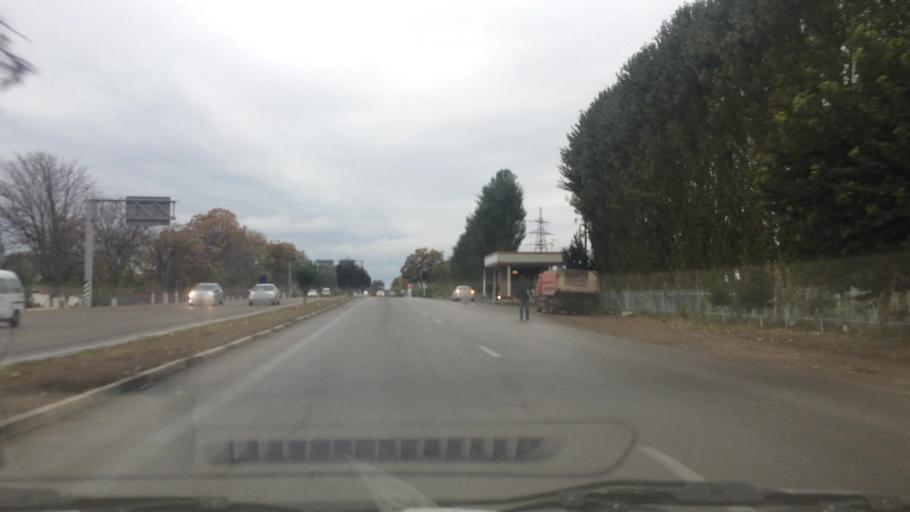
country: UZ
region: Toshkent
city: Yangiyul
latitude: 41.1417
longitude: 69.0242
